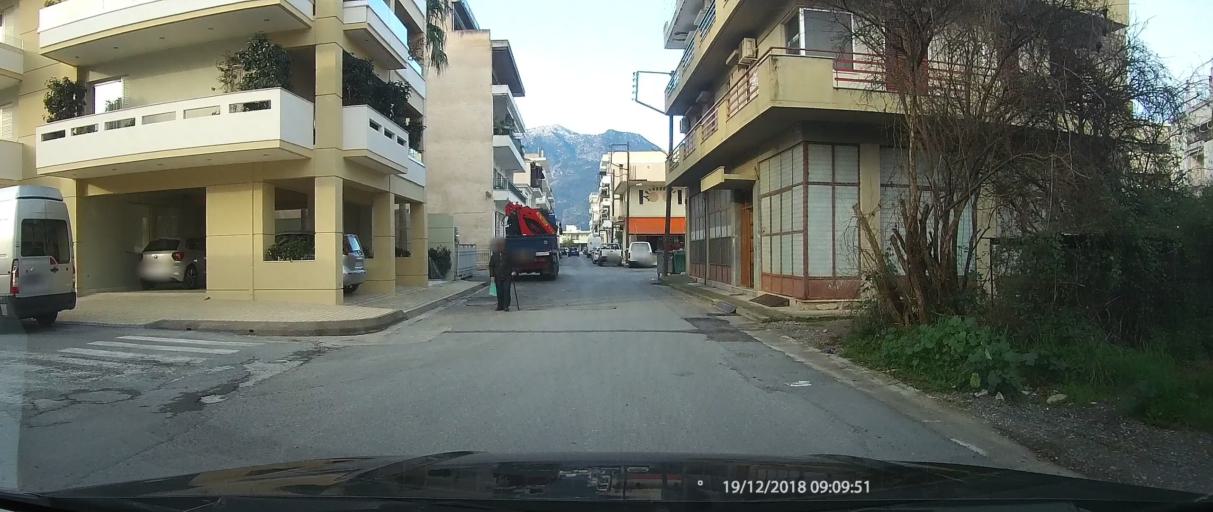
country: GR
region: Peloponnese
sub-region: Nomos Lakonias
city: Sparti
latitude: 37.0752
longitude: 22.4226
